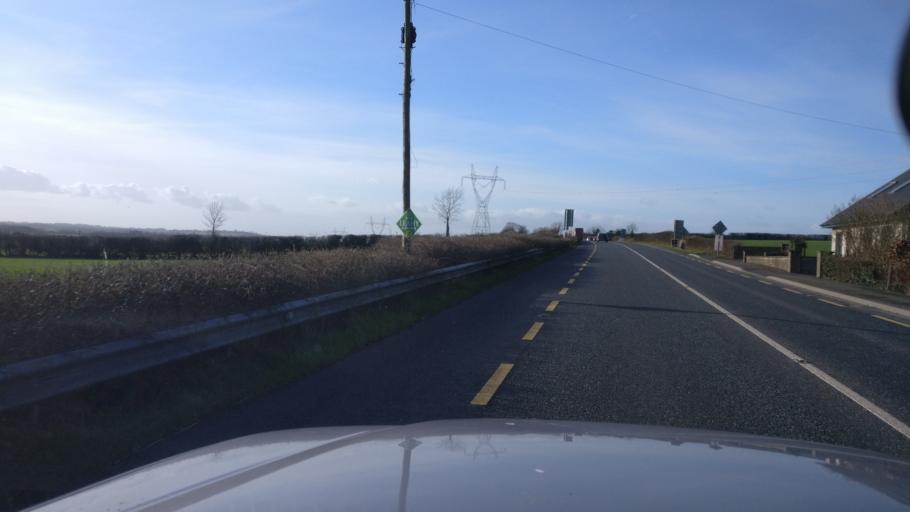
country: IE
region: Leinster
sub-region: Uibh Fhaili
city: Tullamore
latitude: 53.2163
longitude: -7.4579
